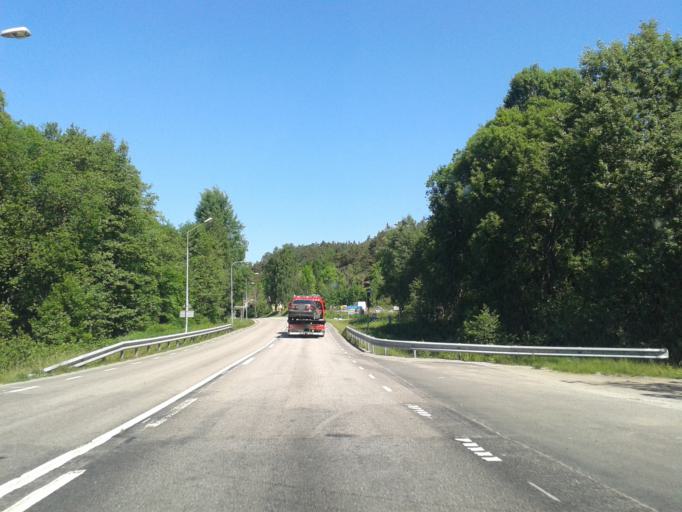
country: SE
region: Vaestra Goetaland
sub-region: Orust
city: Henan
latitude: 58.2278
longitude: 11.6851
